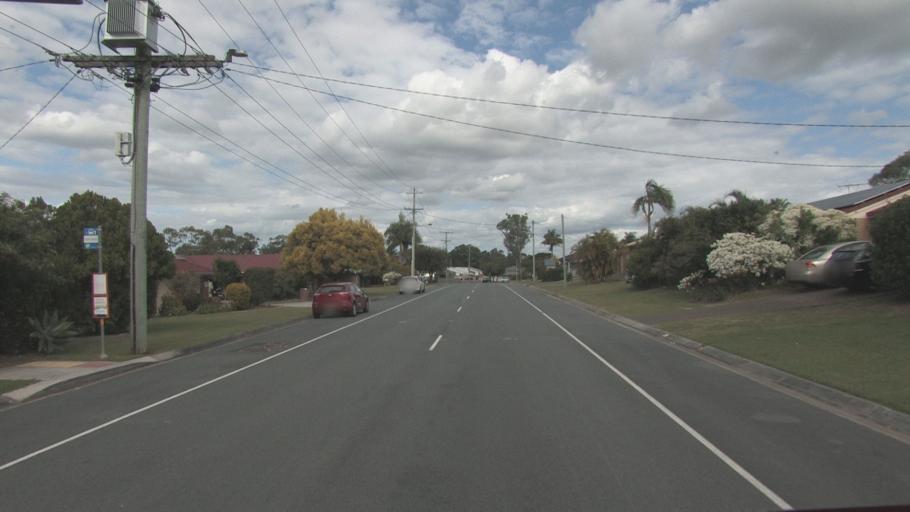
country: AU
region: Queensland
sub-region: Logan
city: Windaroo
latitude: -27.7299
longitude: 153.2128
